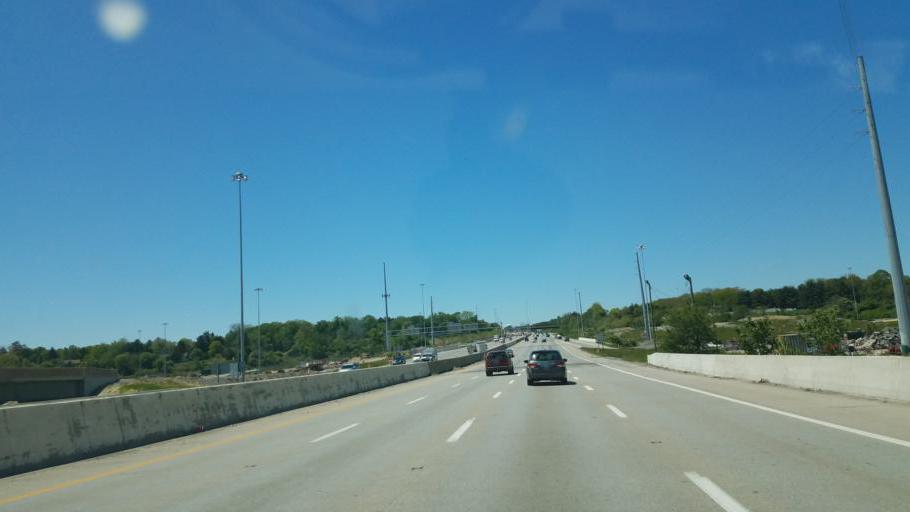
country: US
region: Ohio
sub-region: Franklin County
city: Worthington
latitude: 40.1123
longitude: -83.0318
